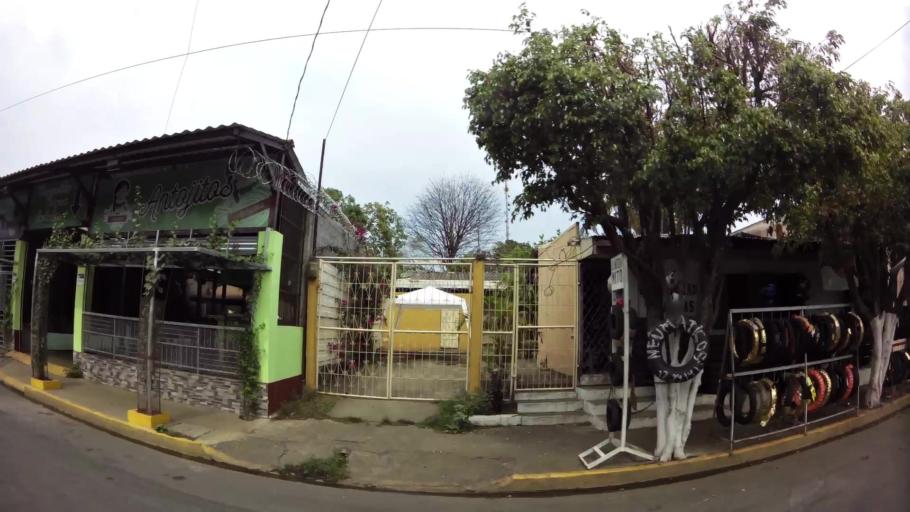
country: NI
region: Masaya
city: Masaya
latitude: 11.9848
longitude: -86.0968
